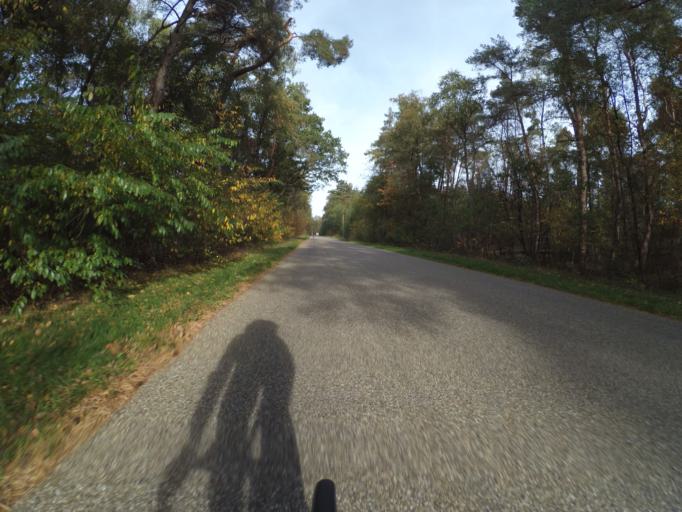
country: NL
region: Overijssel
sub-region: Gemeente Hof van Twente
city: Markelo
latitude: 52.3024
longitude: 6.4199
